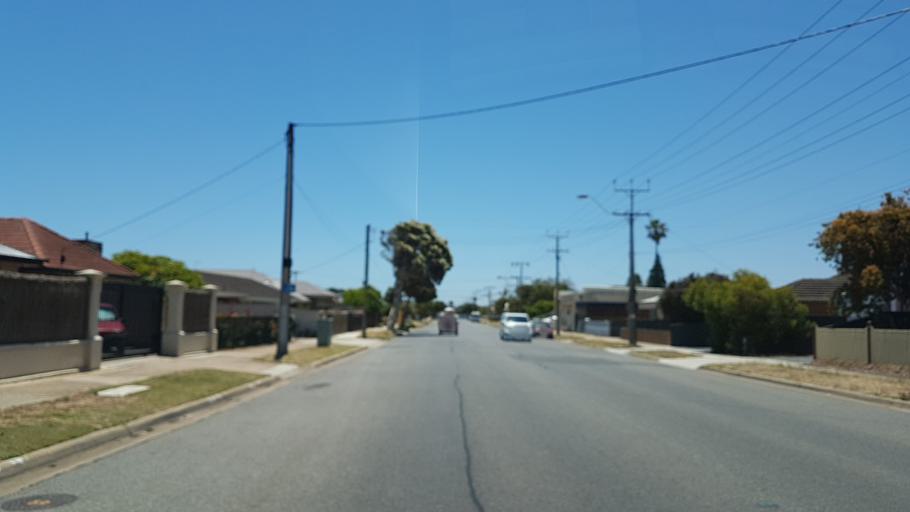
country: AU
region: South Australia
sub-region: Charles Sturt
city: West Lakes Shore
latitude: -34.8552
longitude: 138.4837
